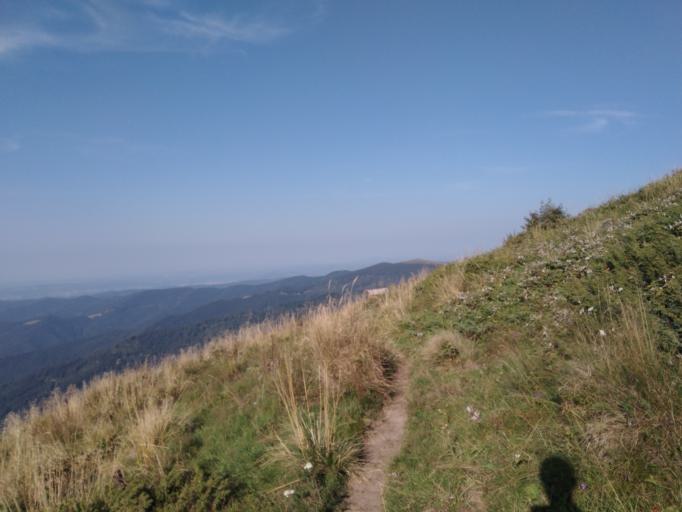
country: BG
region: Stara Zagora
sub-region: Obshtina Pavel Banya
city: Asen
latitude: 42.7623
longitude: 25.1063
